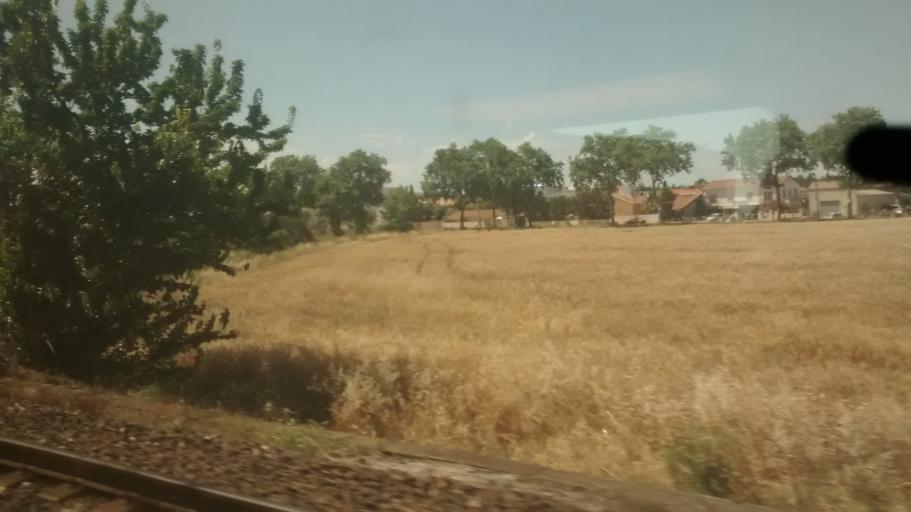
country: FR
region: Languedoc-Roussillon
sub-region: Departement de l'Herault
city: Baillargues
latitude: 43.6593
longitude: 4.0240
